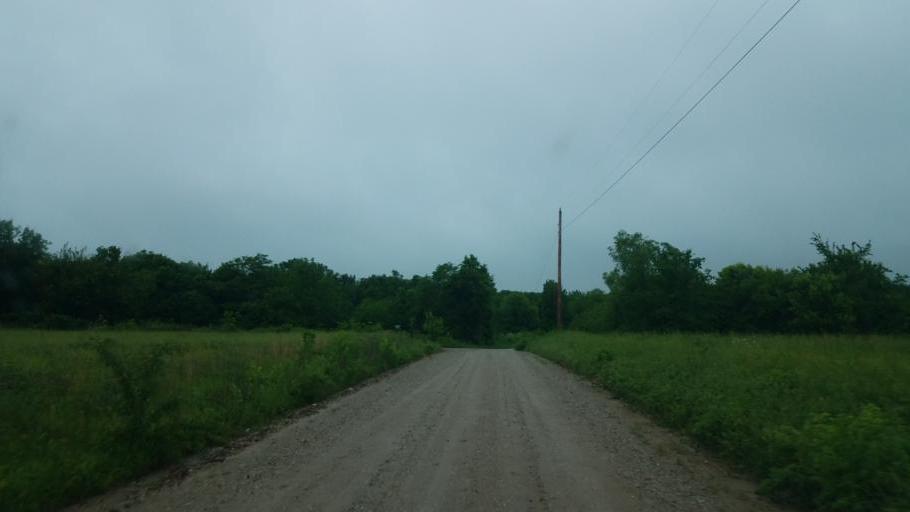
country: US
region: Missouri
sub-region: Moniteau County
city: California
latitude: 38.7358
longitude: -92.6092
